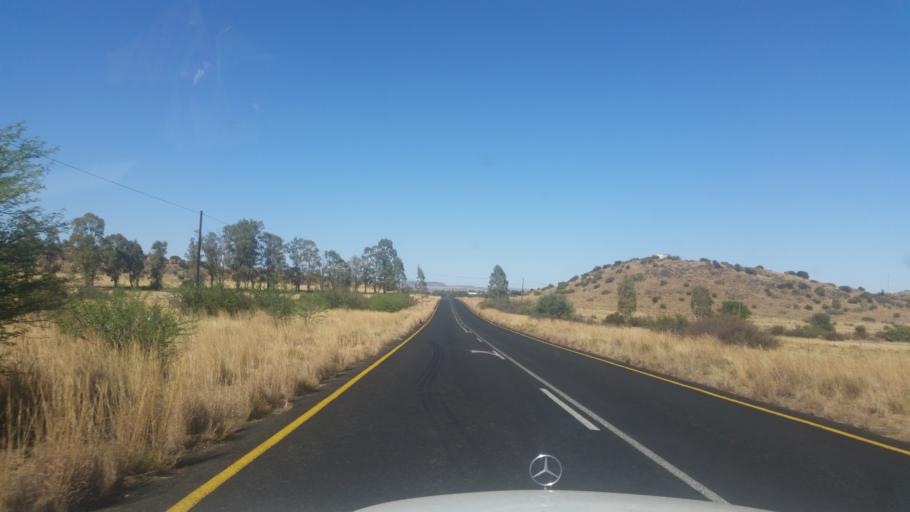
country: ZA
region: Orange Free State
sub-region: Xhariep District Municipality
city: Trompsburg
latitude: -30.4836
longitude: 25.9976
